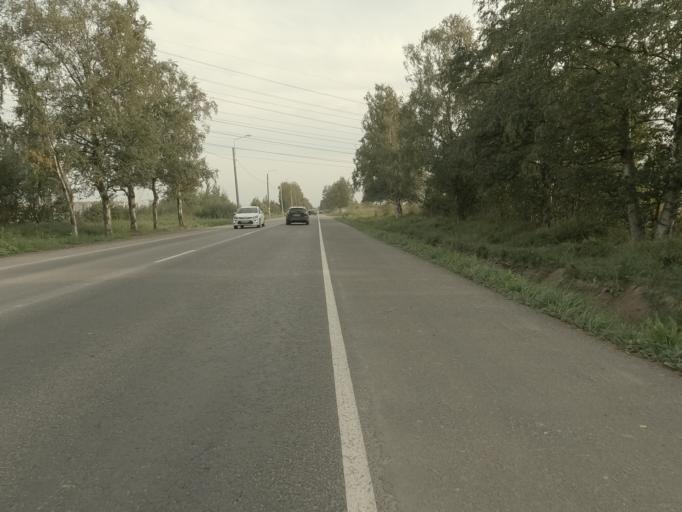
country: RU
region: St.-Petersburg
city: Strel'na
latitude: 59.8492
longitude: 30.0907
